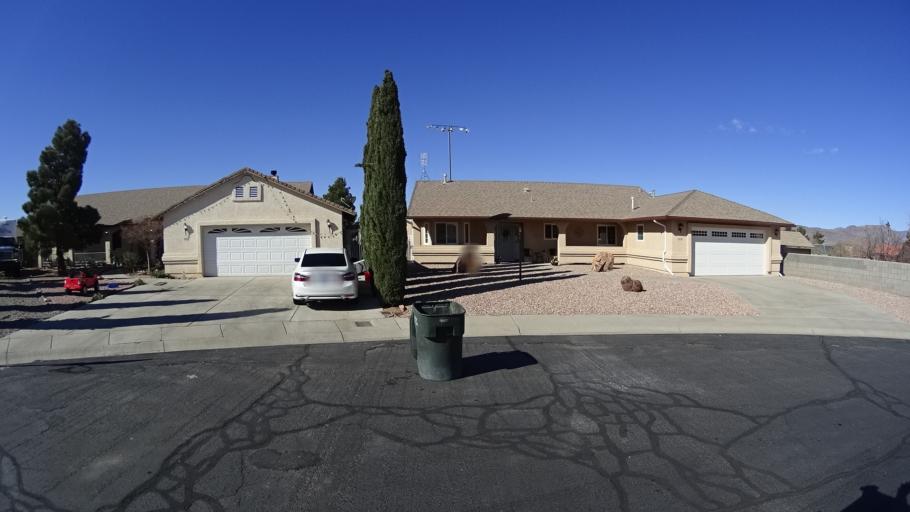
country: US
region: Arizona
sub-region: Mohave County
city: Kingman
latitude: 35.1945
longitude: -114.0088
